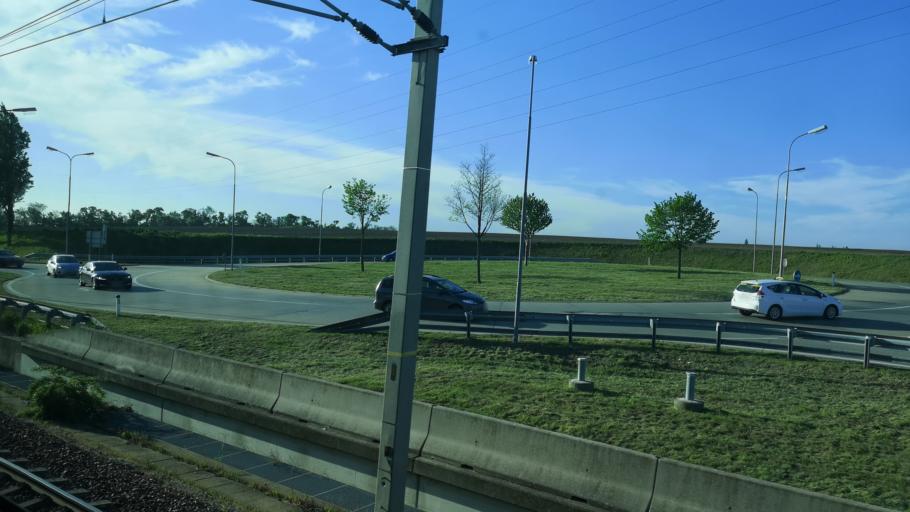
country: AT
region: Lower Austria
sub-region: Politischer Bezirk Wien-Umgebung
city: Schwechat
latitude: 48.1383
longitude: 16.4995
